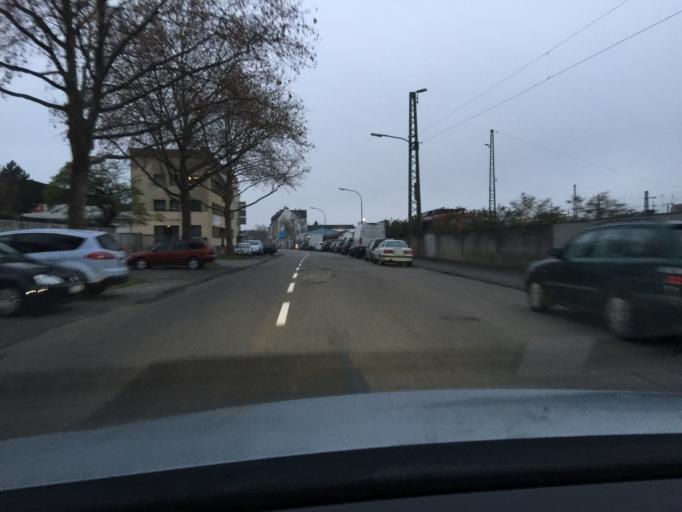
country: DE
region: Rheinland-Pfalz
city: Koblenz
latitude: 50.3710
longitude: 7.5943
